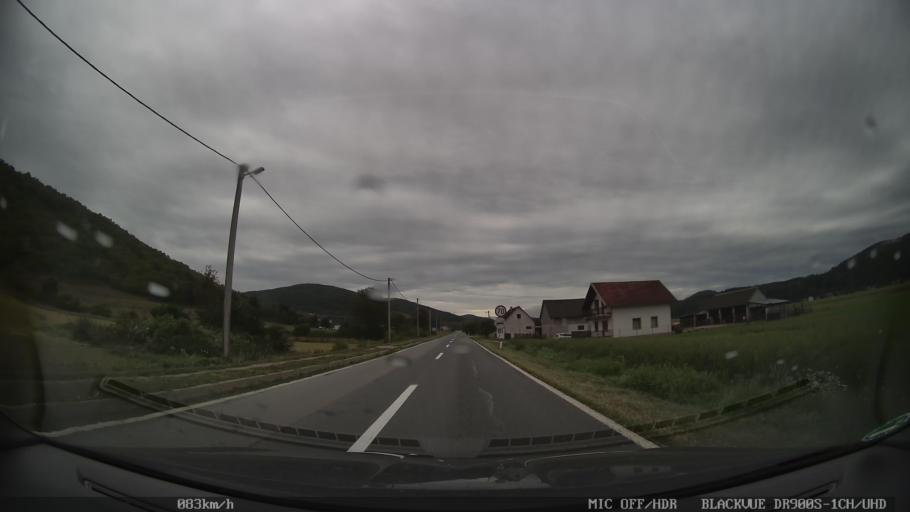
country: HR
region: Licko-Senjska
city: Otocac
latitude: 44.9140
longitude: 15.1593
